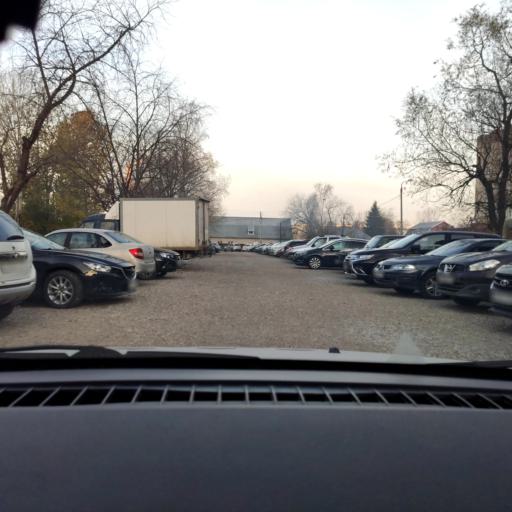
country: RU
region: Perm
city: Perm
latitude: 58.0670
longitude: 56.3412
